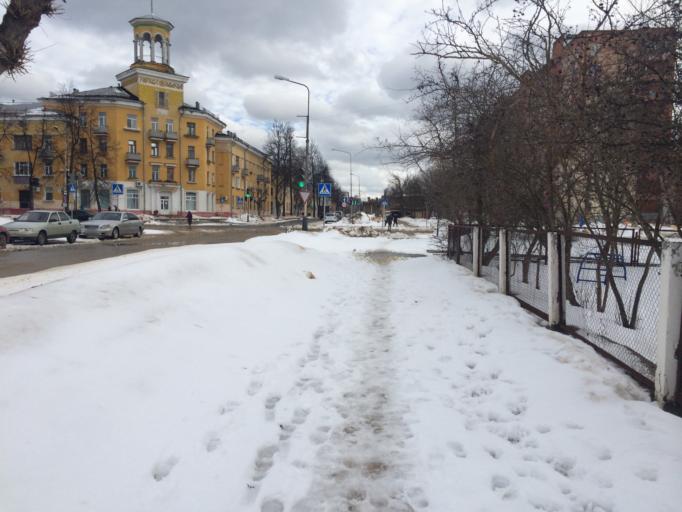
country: RU
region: Nizjnij Novgorod
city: Sarov
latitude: 54.9163
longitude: 43.3402
